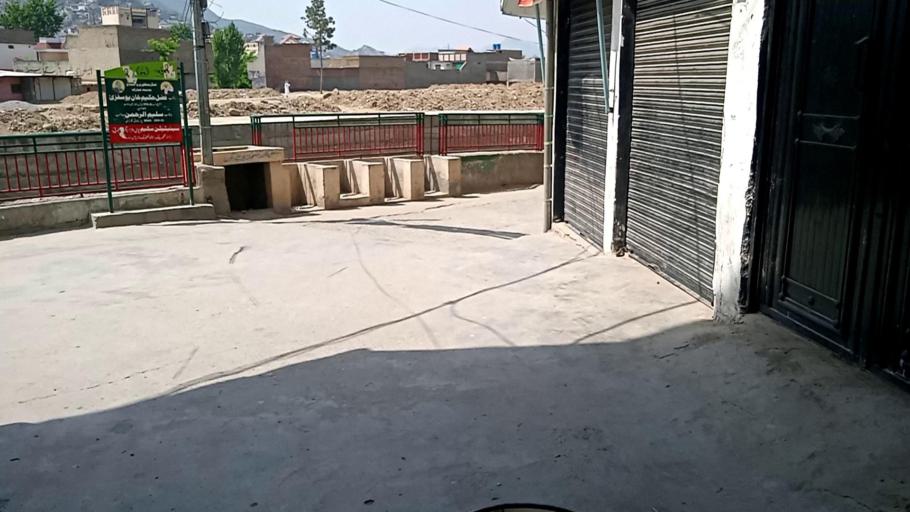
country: PK
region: Khyber Pakhtunkhwa
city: Mingora
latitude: 34.7756
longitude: 72.3549
